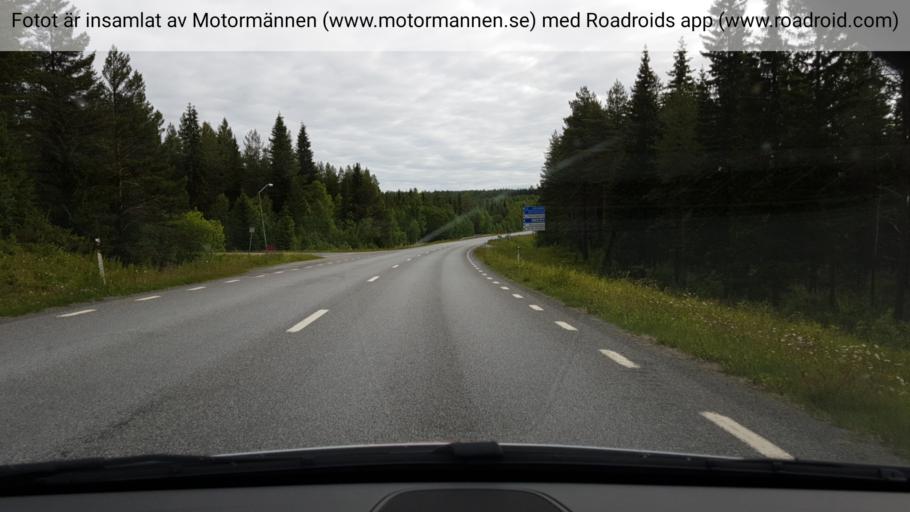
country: SE
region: Jaemtland
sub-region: OEstersunds Kommun
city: Lit
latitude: 63.3960
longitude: 14.9747
